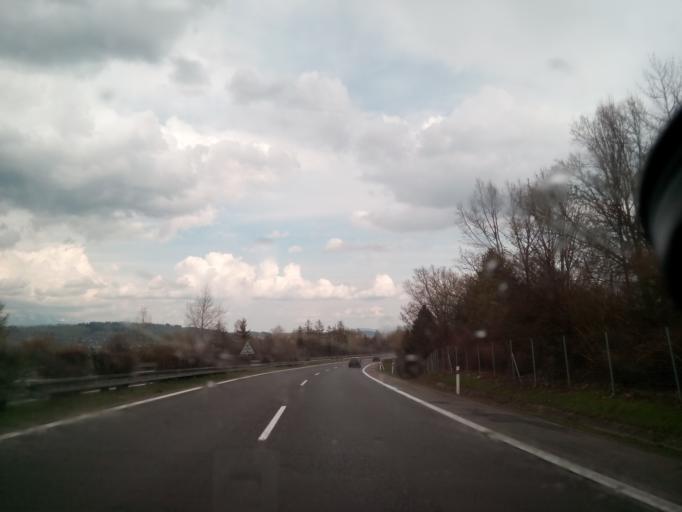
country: SK
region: Zilinsky
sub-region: Okres Liptovsky Mikulas
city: Liptovsky Mikulas
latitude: 49.0822
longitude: 19.5805
